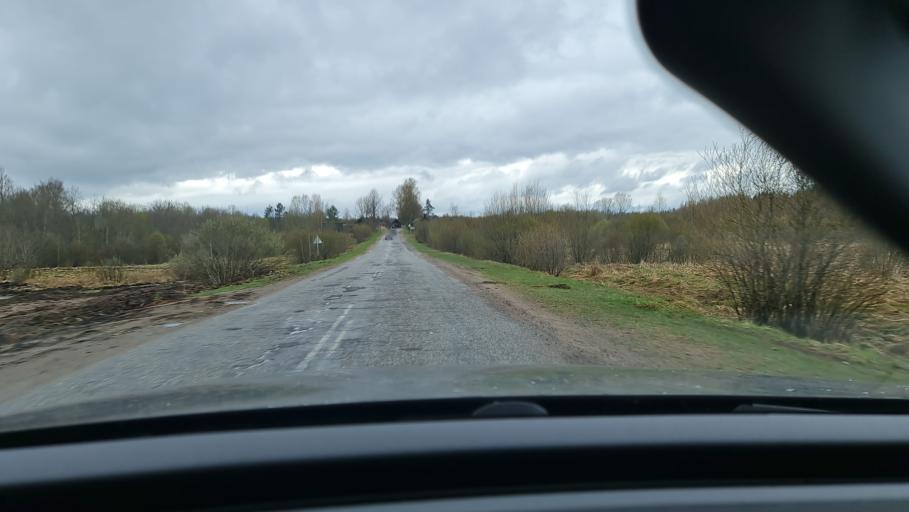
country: RU
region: Novgorod
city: Marevo
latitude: 57.2436
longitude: 32.0522
